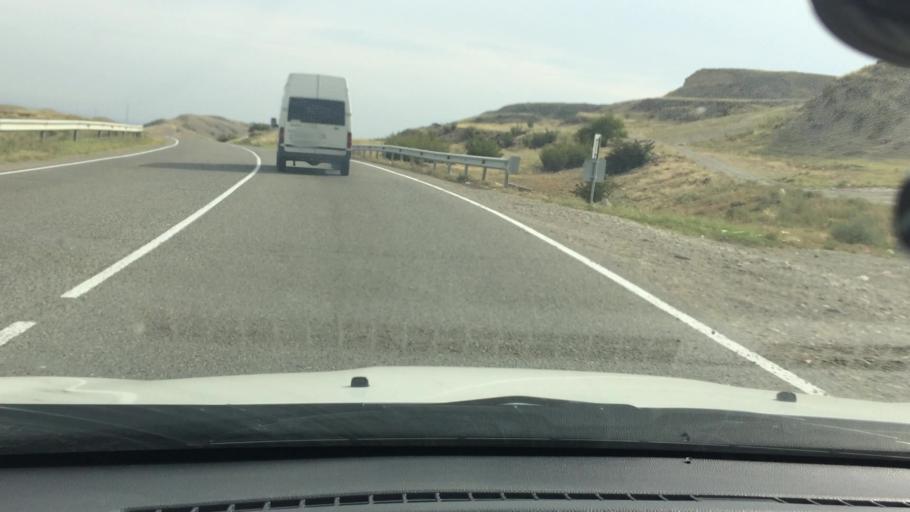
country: GE
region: Kvemo Kartli
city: Rust'avi
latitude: 41.5368
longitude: 44.9785
